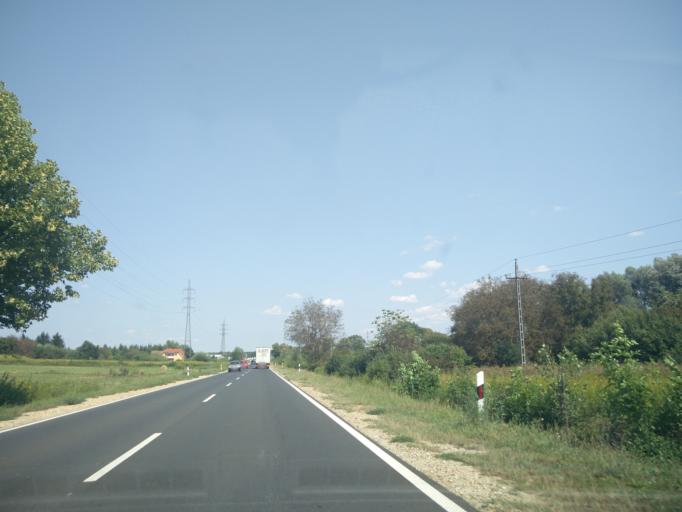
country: HU
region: Zala
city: Zalaegerszeg
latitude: 46.8324
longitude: 16.8641
